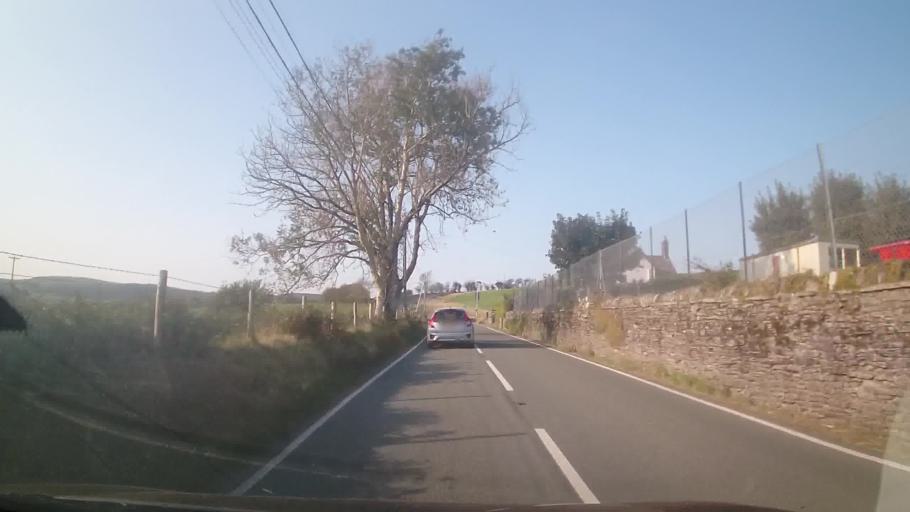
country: GB
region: Wales
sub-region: County of Ceredigion
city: Lledrod
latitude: 52.2891
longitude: -3.8610
